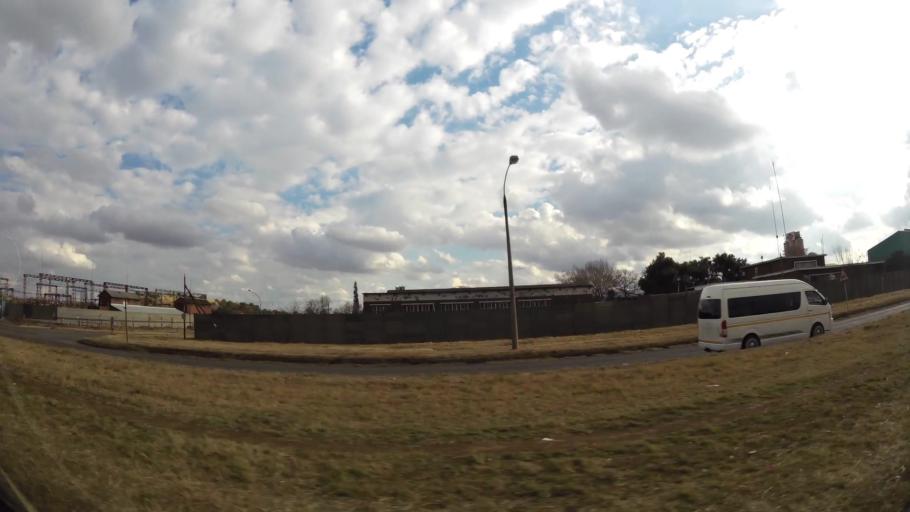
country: ZA
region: Orange Free State
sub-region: Fezile Dabi District Municipality
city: Sasolburg
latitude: -26.8239
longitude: 27.8364
